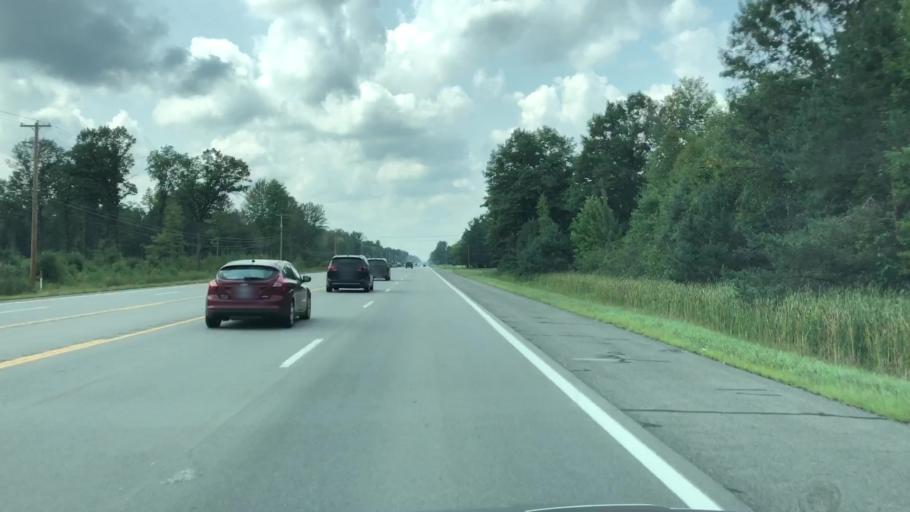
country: US
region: Michigan
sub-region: Midland County
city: Coleman
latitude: 43.6113
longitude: -84.4600
